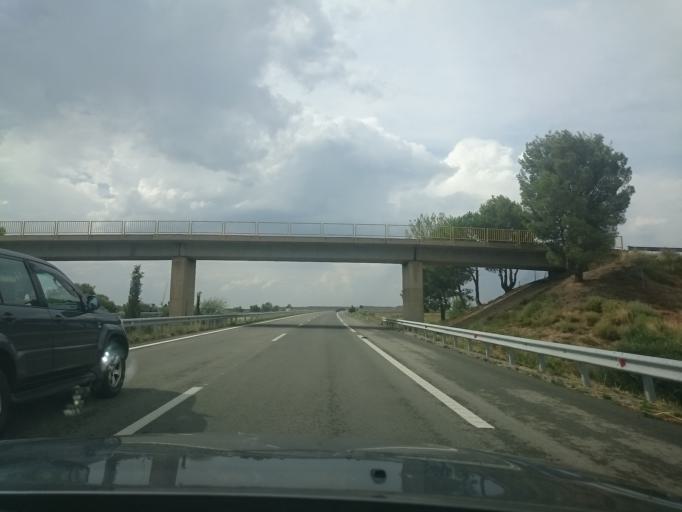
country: ES
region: La Rioja
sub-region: Provincia de La Rioja
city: Rincon de Soto
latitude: 42.1770
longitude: -1.8363
